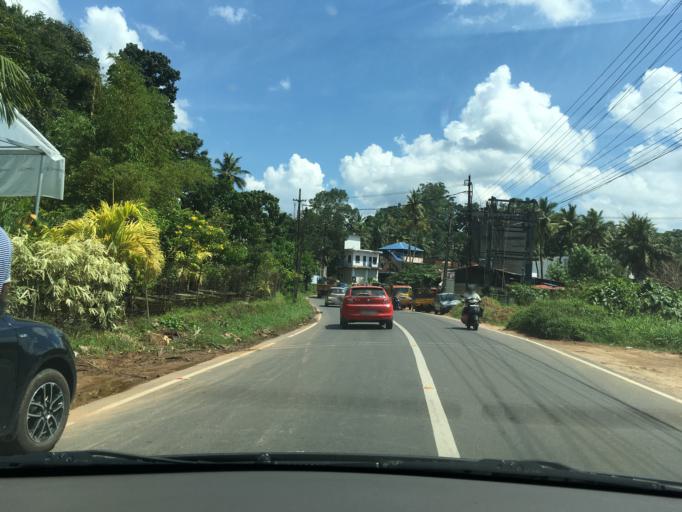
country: IN
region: Kerala
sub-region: Thiruvananthapuram
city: Nedumangad
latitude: 8.6083
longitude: 76.9983
